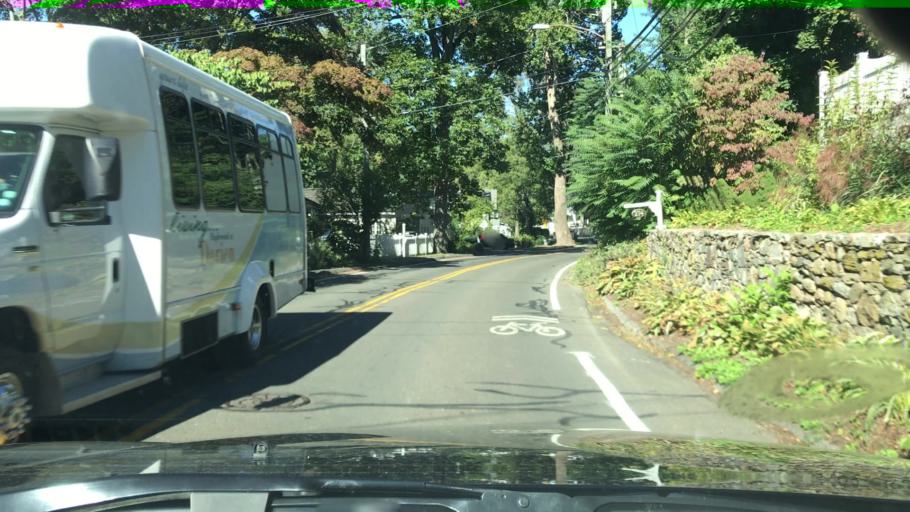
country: US
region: Connecticut
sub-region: Fairfield County
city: Darien
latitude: 41.0752
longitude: -73.4459
